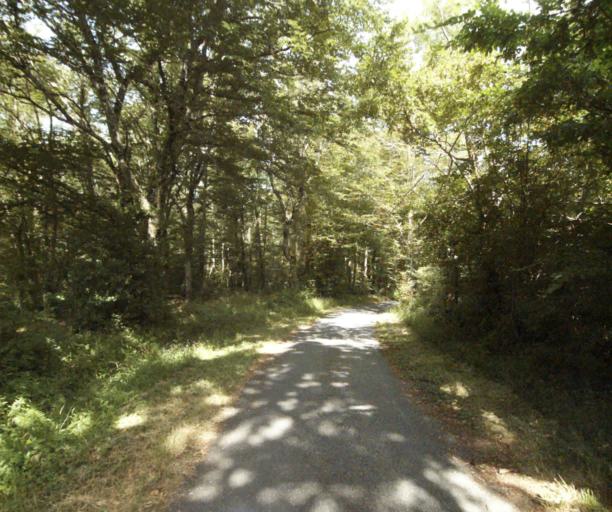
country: FR
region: Midi-Pyrenees
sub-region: Departement du Tarn
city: Soreze
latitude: 43.4623
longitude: 2.0959
